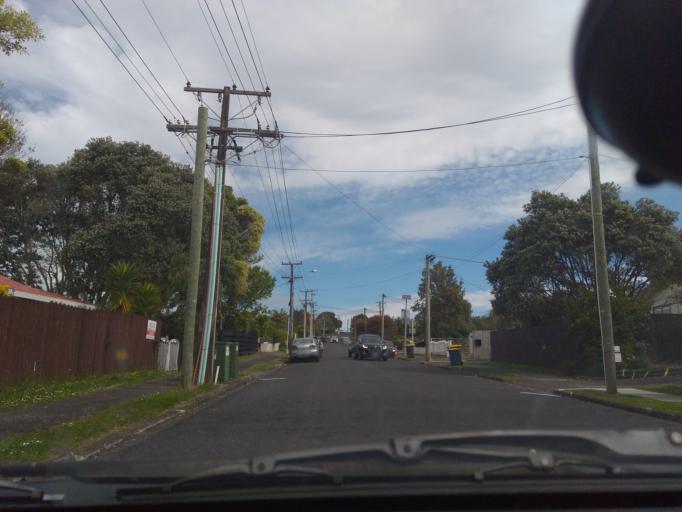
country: NZ
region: Auckland
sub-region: Auckland
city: Waitakere
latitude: -36.9232
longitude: 174.6754
